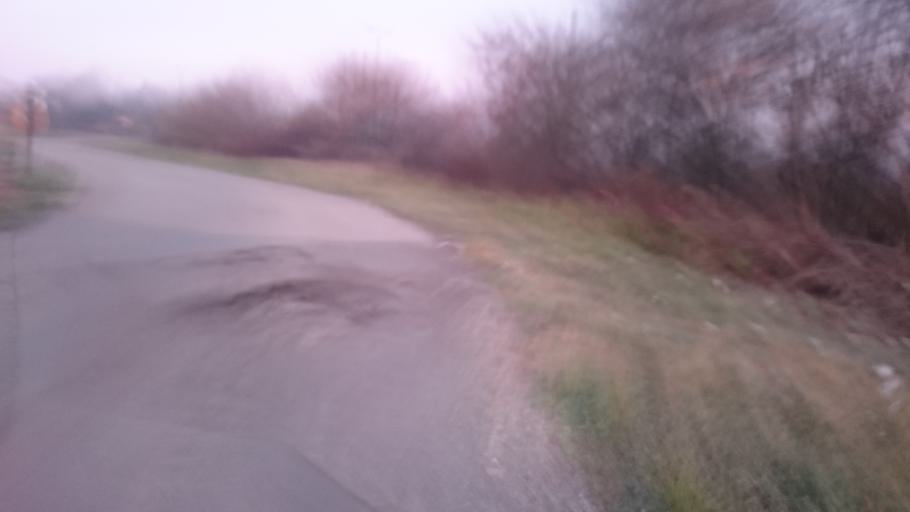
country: PL
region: Lesser Poland Voivodeship
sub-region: Powiat wielicki
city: Czarnochowice
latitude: 50.0278
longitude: 20.0038
